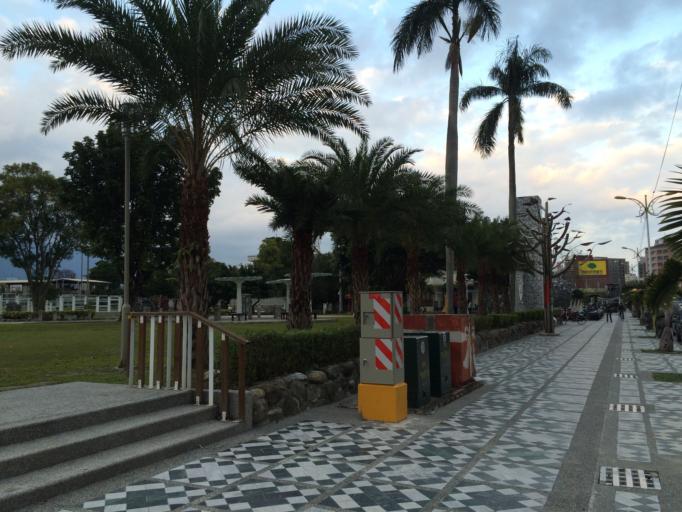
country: TW
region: Taiwan
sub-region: Hualien
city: Hualian
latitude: 23.9895
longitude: 121.6008
